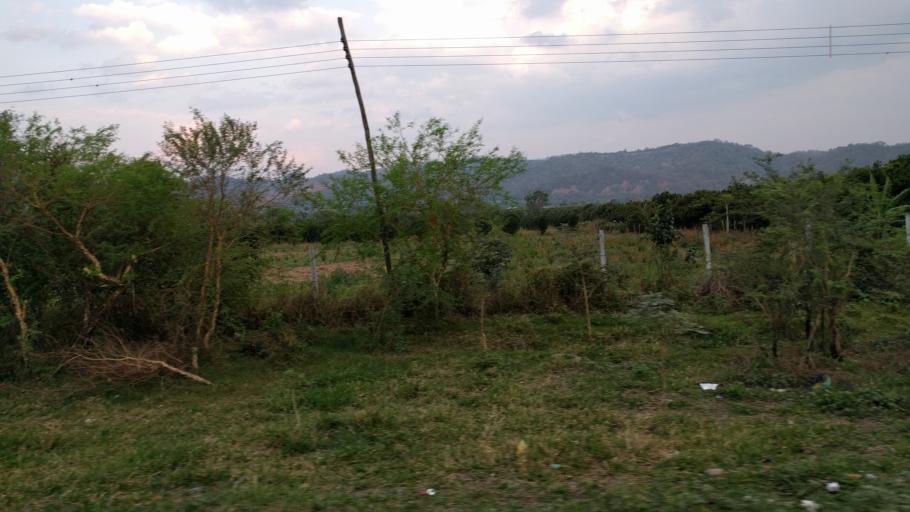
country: BO
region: Santa Cruz
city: Jorochito
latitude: -18.1339
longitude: -63.4728
